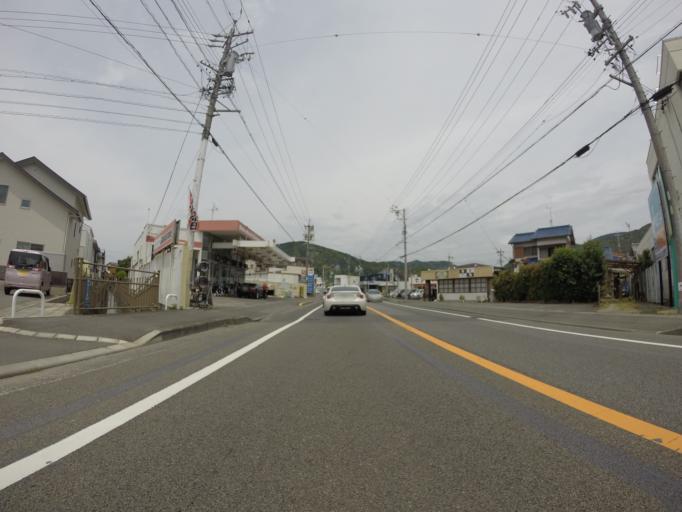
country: JP
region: Shizuoka
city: Shizuoka-shi
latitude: 34.9829
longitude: 138.3355
